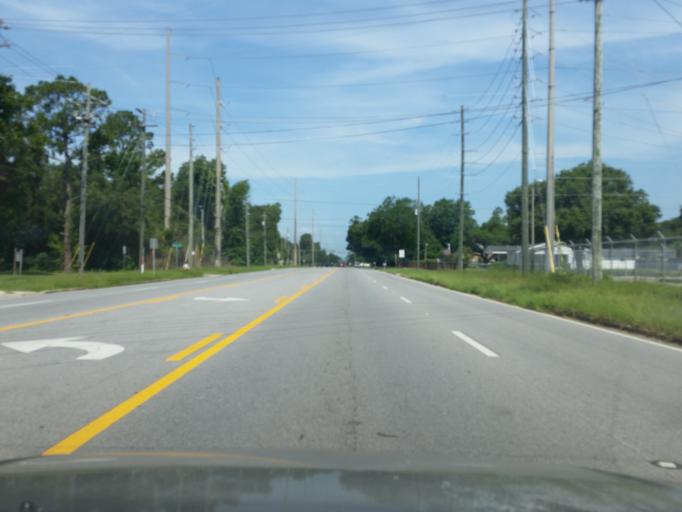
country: US
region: Florida
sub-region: Escambia County
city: Ferry Pass
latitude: 30.5288
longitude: -87.2051
